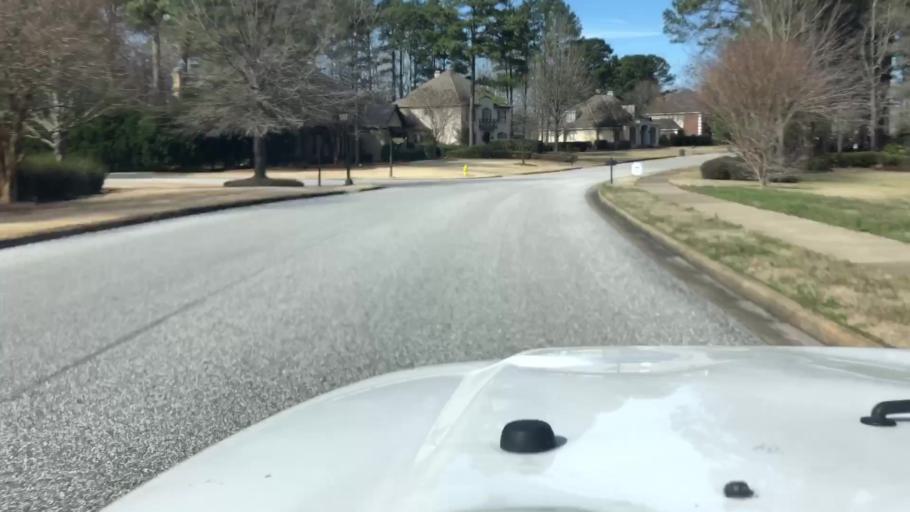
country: US
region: Alabama
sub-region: Montgomery County
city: Pike Road
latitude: 32.3564
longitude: -86.1515
